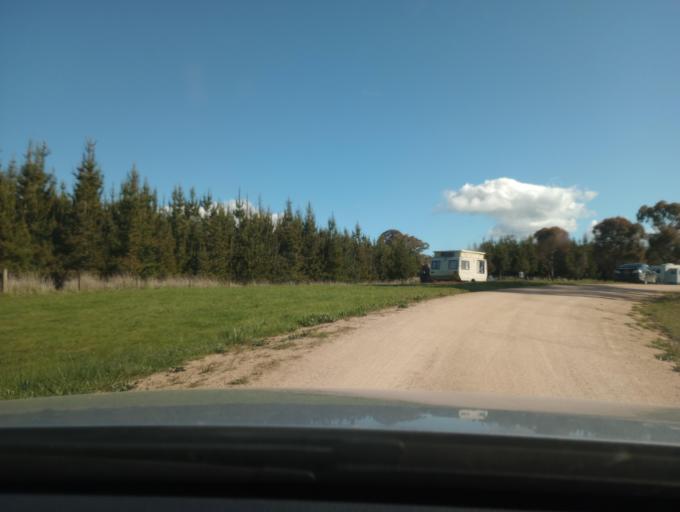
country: AU
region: New South Wales
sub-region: Blayney
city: Millthorpe
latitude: -33.4098
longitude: 149.3139
